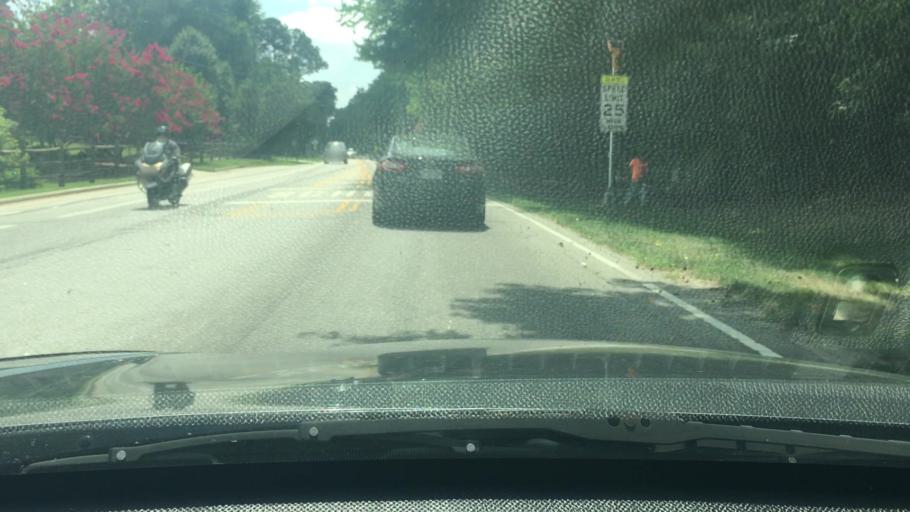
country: US
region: North Carolina
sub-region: Wake County
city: Cary
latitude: 35.7953
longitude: -78.7924
